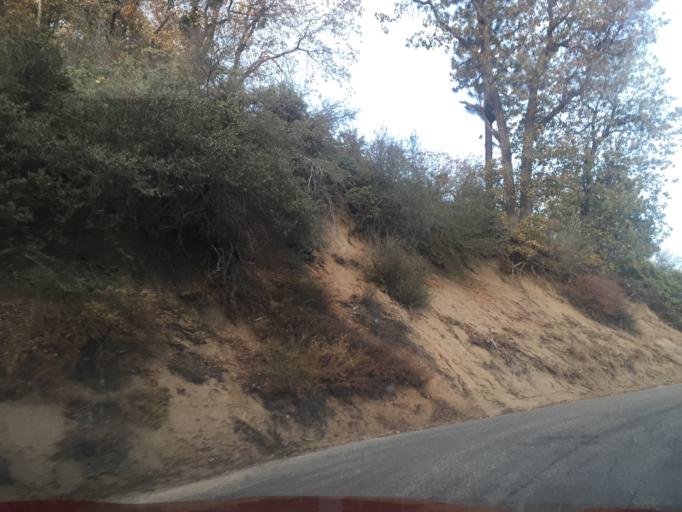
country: US
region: California
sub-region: Tulare County
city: Three Rivers
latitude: 36.4505
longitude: -118.6951
